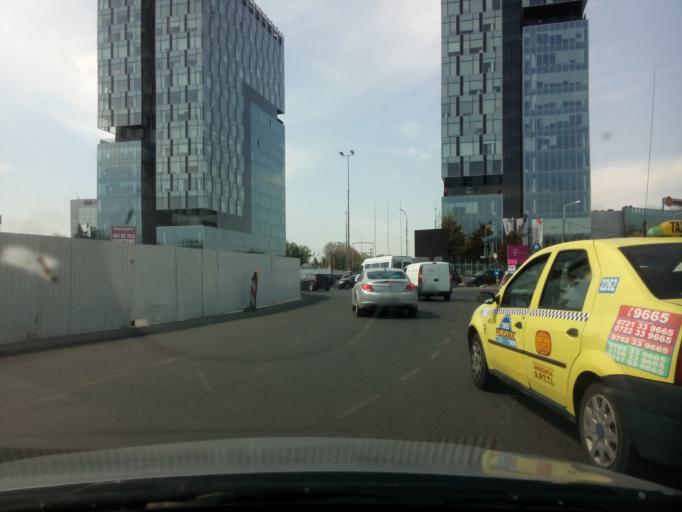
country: RO
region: Bucuresti
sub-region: Municipiul Bucuresti
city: Bucuresti
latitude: 44.4785
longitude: 26.0728
